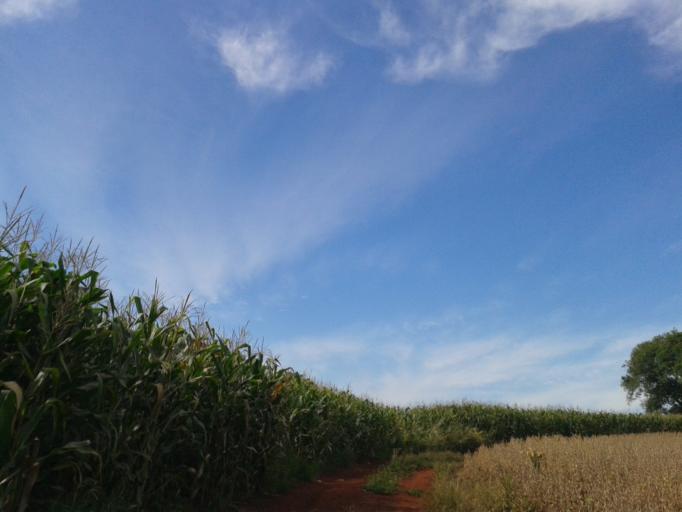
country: BR
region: Minas Gerais
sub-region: Capinopolis
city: Capinopolis
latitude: -18.6479
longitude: -49.7018
